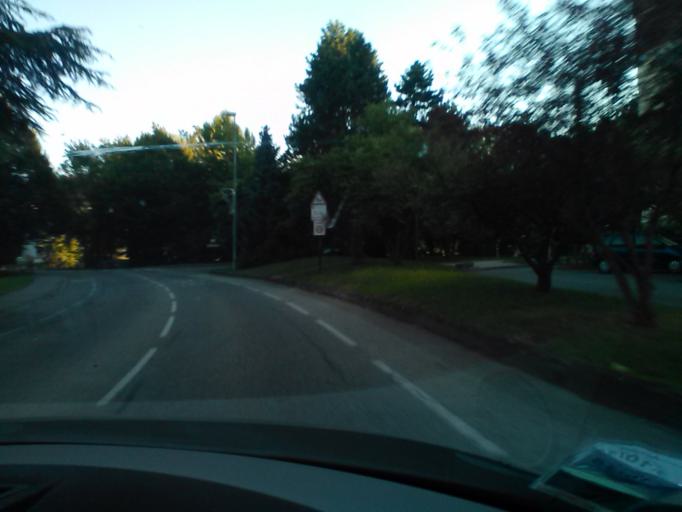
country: FR
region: Rhone-Alpes
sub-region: Departement de la Savoie
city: Chambery
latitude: 45.5621
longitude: 5.9420
